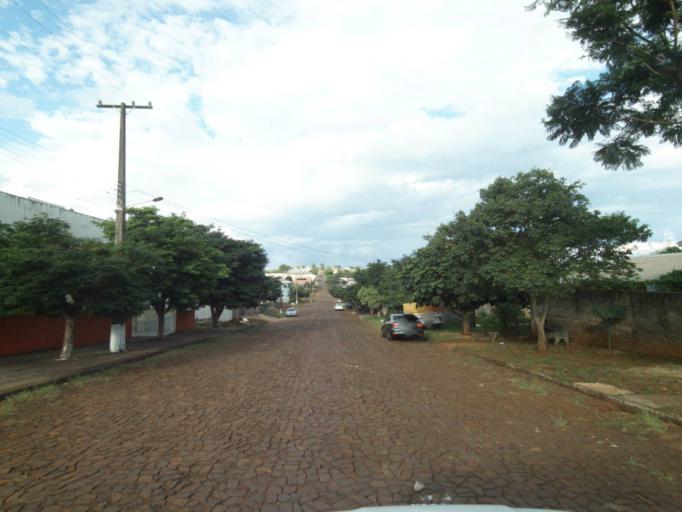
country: BR
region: Parana
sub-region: Laranjeiras Do Sul
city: Laranjeiras do Sul
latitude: -25.4948
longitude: -52.5316
